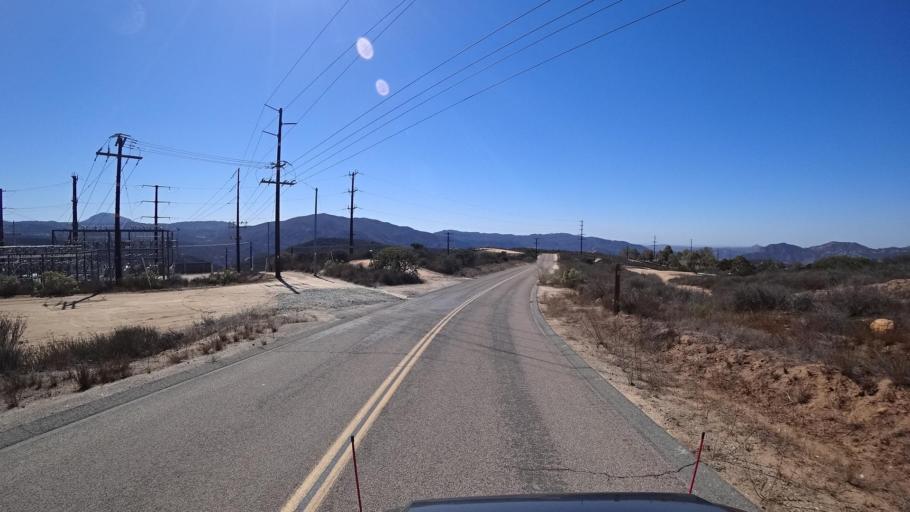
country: US
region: California
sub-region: San Diego County
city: Harbison Canyon
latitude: 32.7976
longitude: -116.7925
